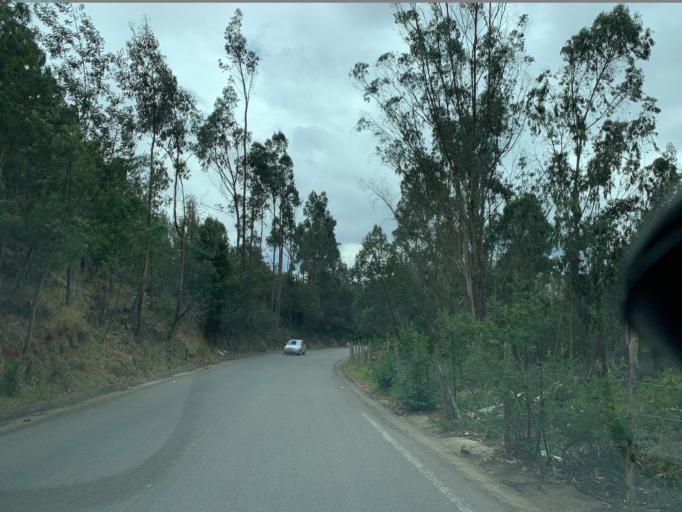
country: CO
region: Boyaca
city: Tunja
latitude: 5.5627
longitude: -73.3624
